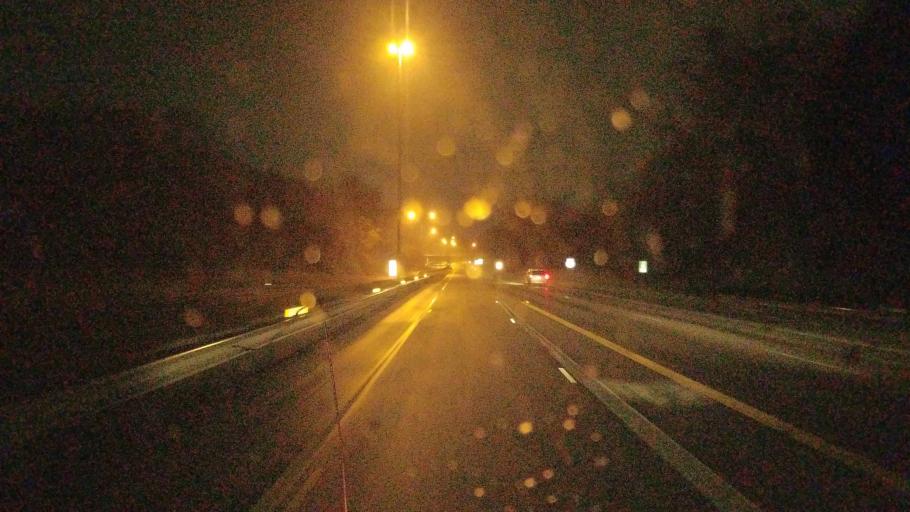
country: US
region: Ohio
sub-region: Lucas County
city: Sylvania
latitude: 41.6877
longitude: -83.6894
